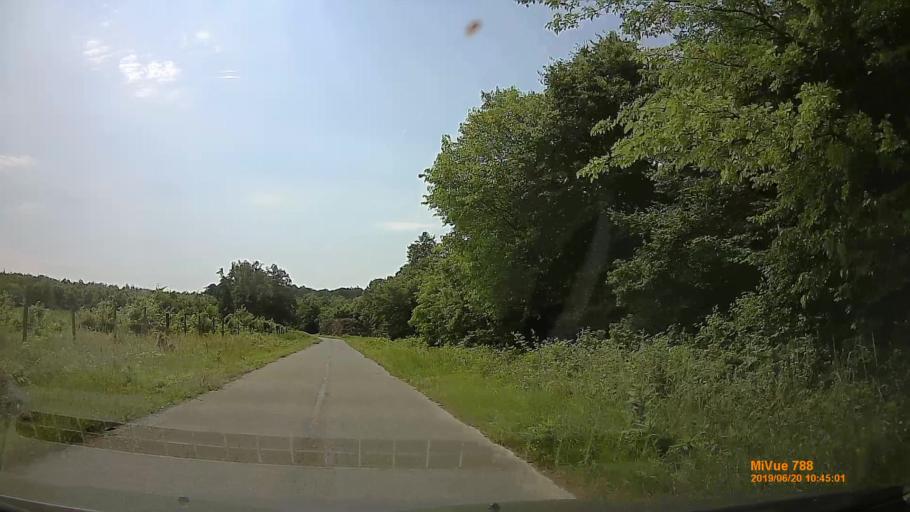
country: HU
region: Baranya
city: Hidas
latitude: 46.1852
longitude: 18.5687
